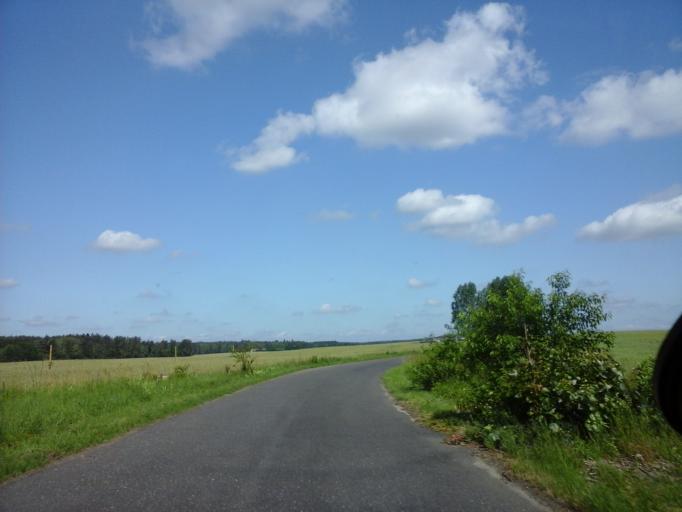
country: PL
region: West Pomeranian Voivodeship
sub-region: Powiat choszczenski
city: Recz
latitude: 53.1996
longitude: 15.5583
